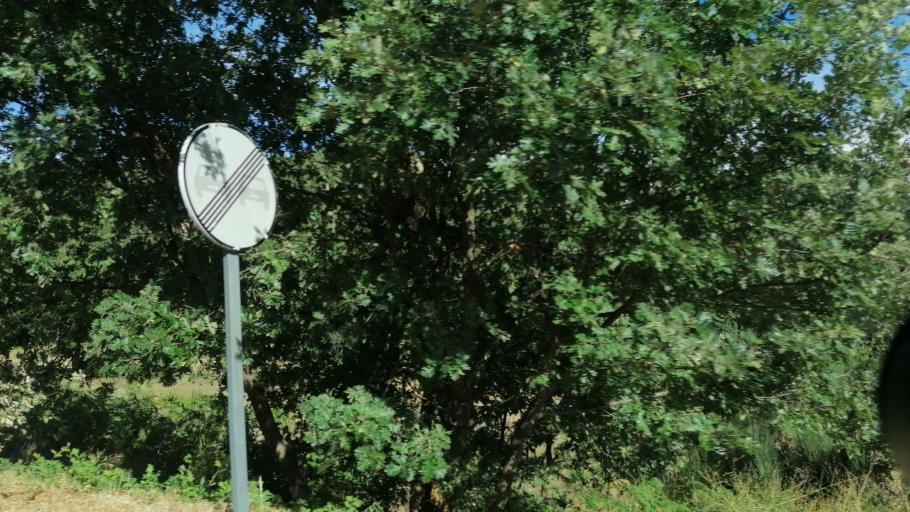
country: PT
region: Vila Real
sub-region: Murca
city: Murca
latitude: 41.3727
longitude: -7.5280
